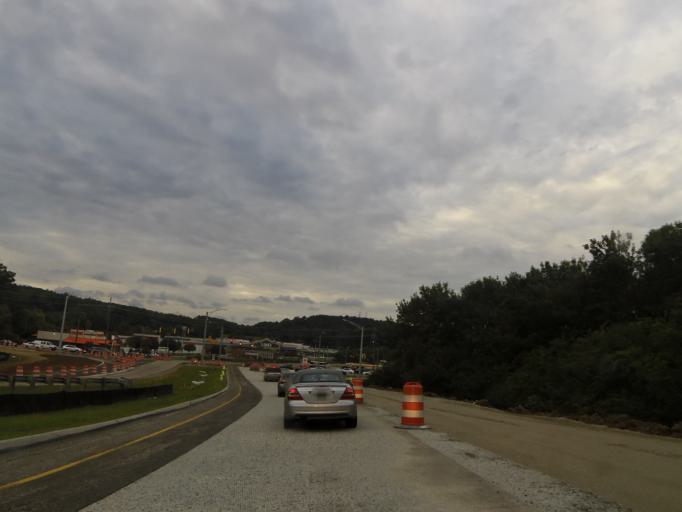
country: US
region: Alabama
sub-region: Jefferson County
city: Trussville
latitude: 33.5936
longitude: -86.6465
